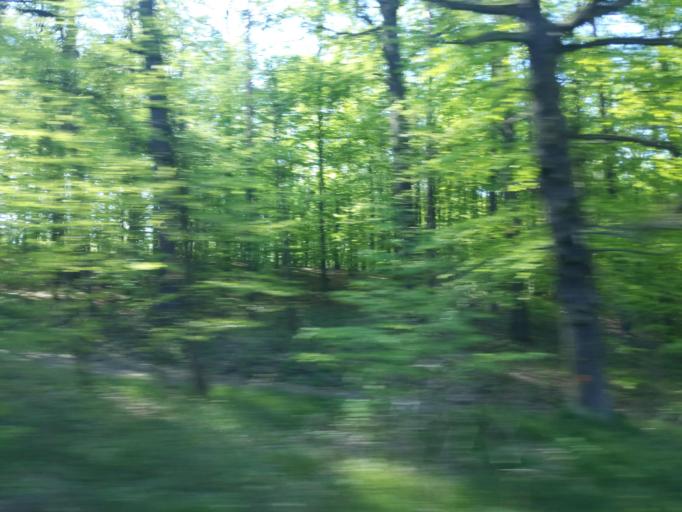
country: DE
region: Saxony
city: Bischofswerda
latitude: 51.1350
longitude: 14.2036
